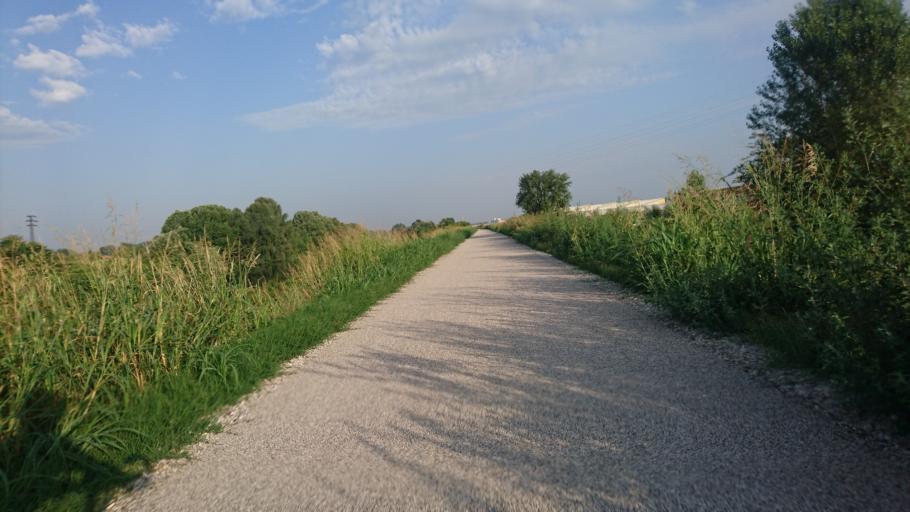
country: IT
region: Veneto
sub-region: Provincia di Padova
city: Oltre Brenta
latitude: 45.4185
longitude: 11.9818
